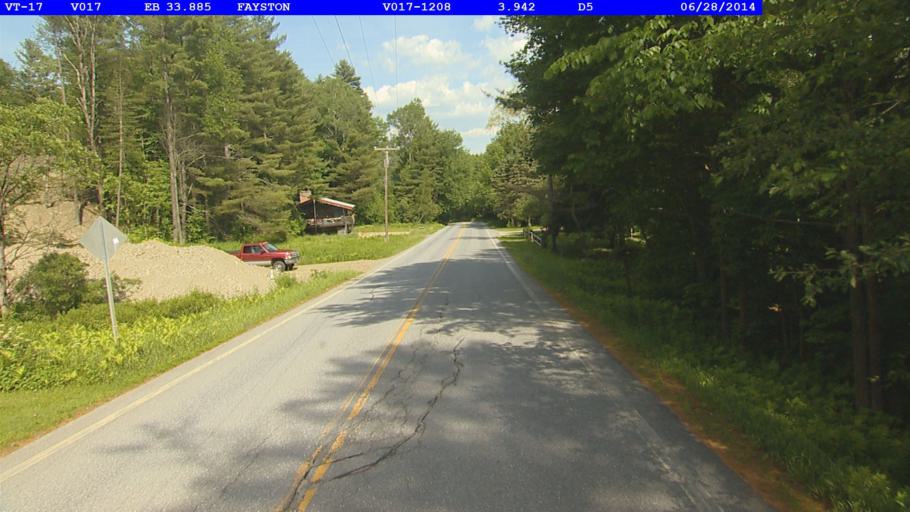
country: US
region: Vermont
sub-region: Washington County
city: Waterbury
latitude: 44.1866
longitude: -72.8775
